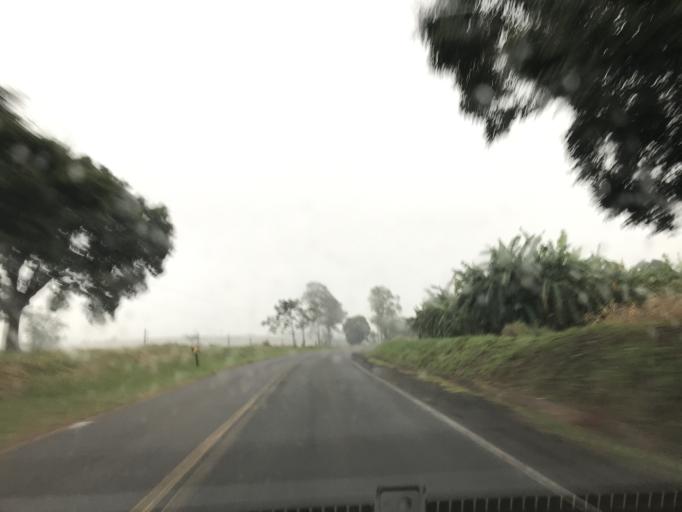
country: PY
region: Canindeyu
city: Salto del Guaira
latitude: -24.1240
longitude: -54.1187
